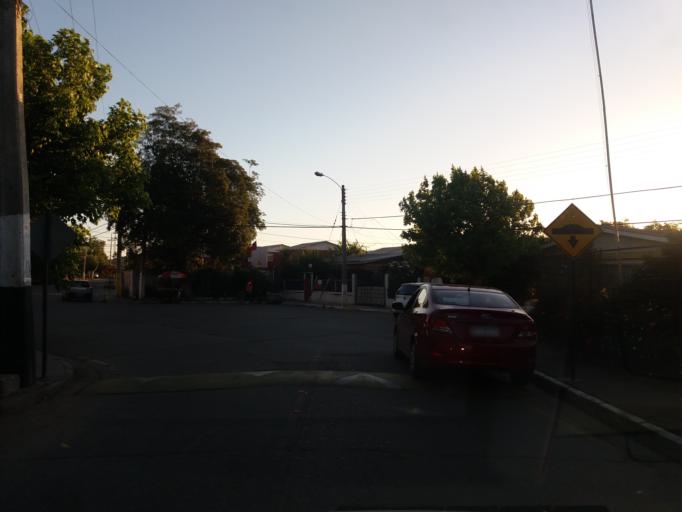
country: CL
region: Valparaiso
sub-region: Provincia de Quillota
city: Quillota
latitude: -32.9381
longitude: -71.2778
